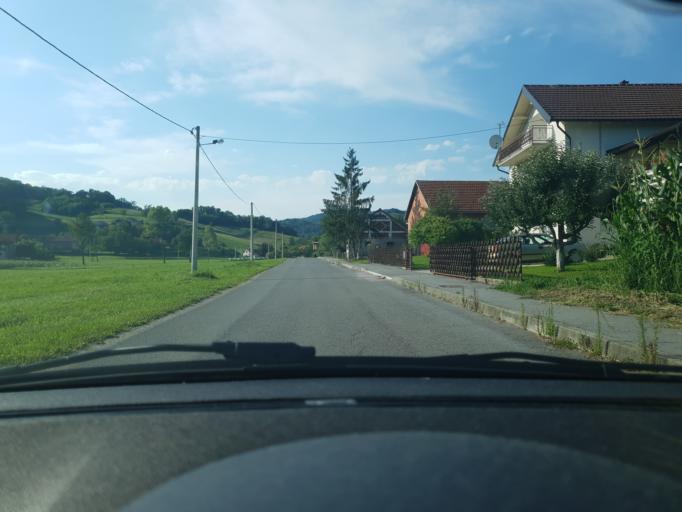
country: HR
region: Krapinsko-Zagorska
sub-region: Grad Krapina
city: Krapina
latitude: 46.1429
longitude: 15.8508
